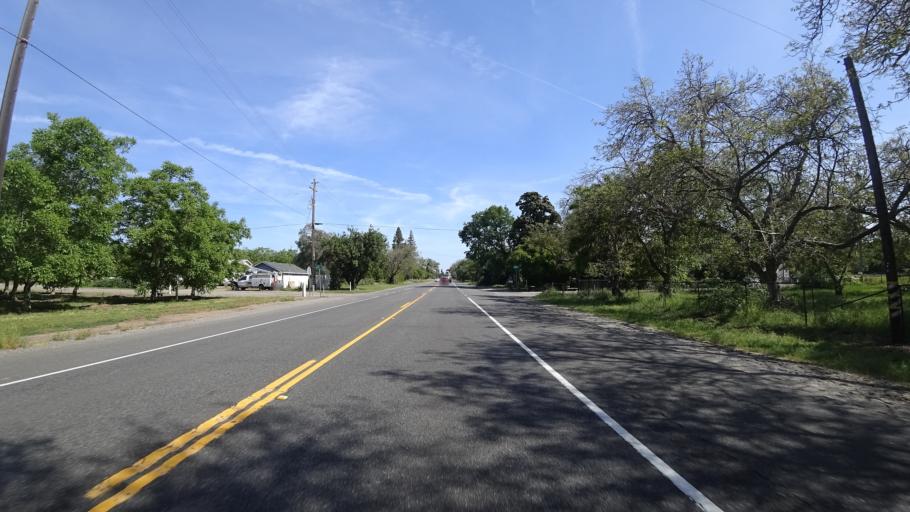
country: US
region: California
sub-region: Tehama County
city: Red Bluff
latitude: 40.1553
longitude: -122.1453
